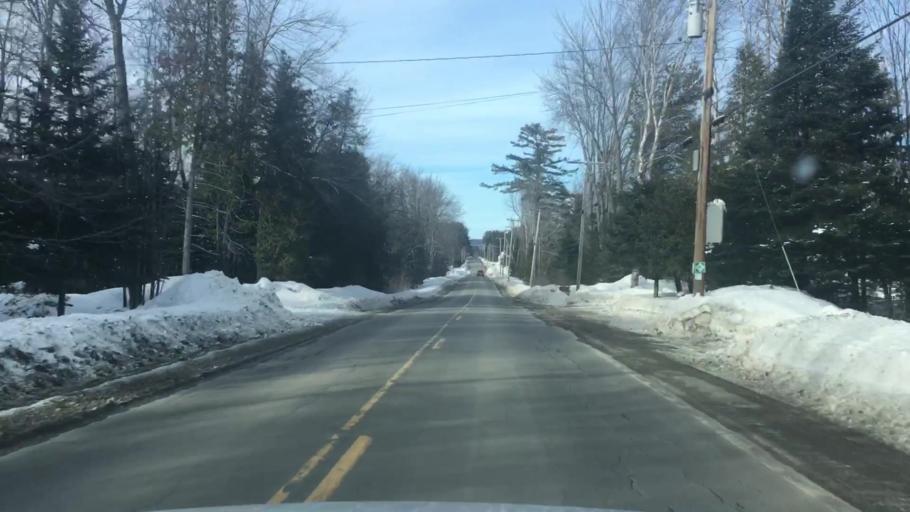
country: US
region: Maine
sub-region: Penobscot County
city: Charleston
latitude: 45.0485
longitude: -69.0294
